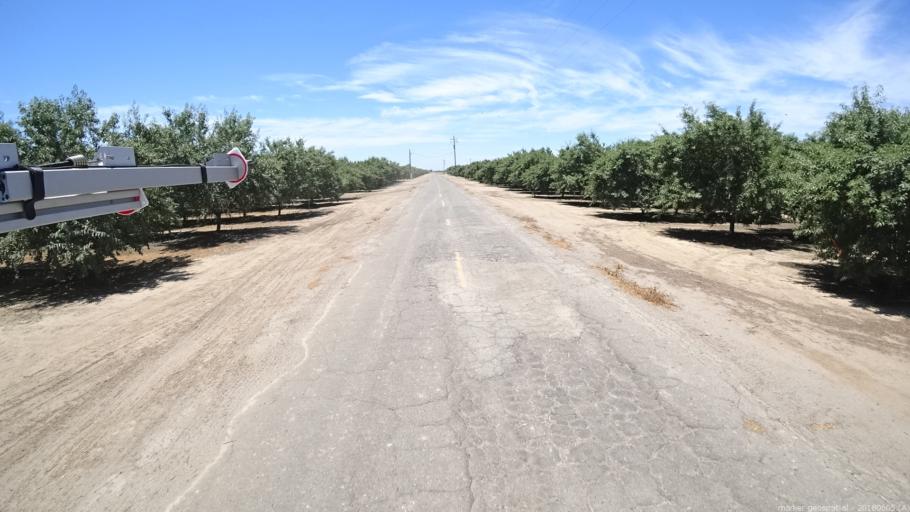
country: US
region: California
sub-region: Madera County
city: Chowchilla
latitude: 37.1055
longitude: -120.2945
